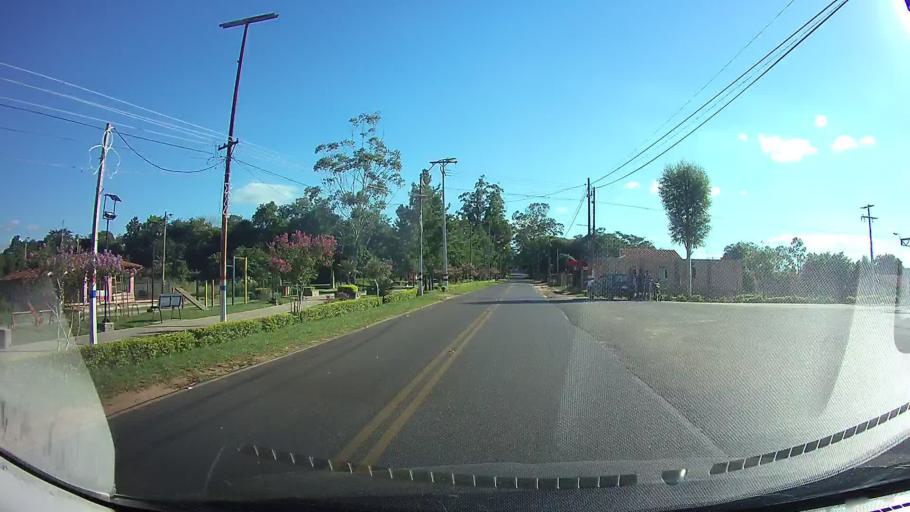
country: PY
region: Cordillera
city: Atyra
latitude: -25.2847
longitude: -57.1772
